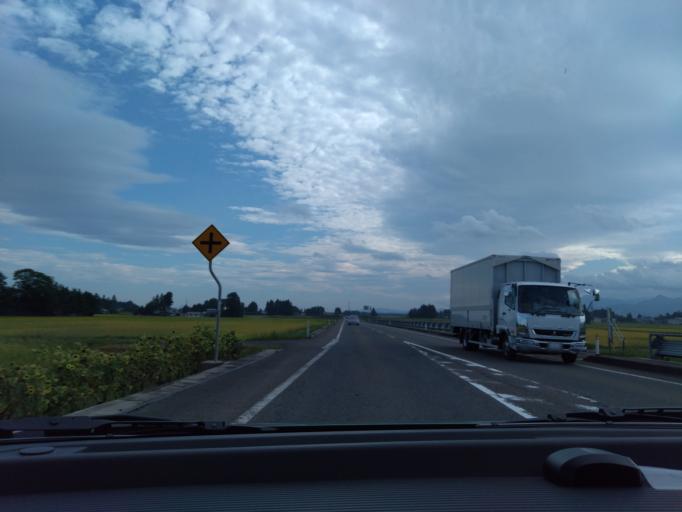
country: JP
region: Iwate
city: Hanamaki
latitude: 39.3562
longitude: 141.0546
